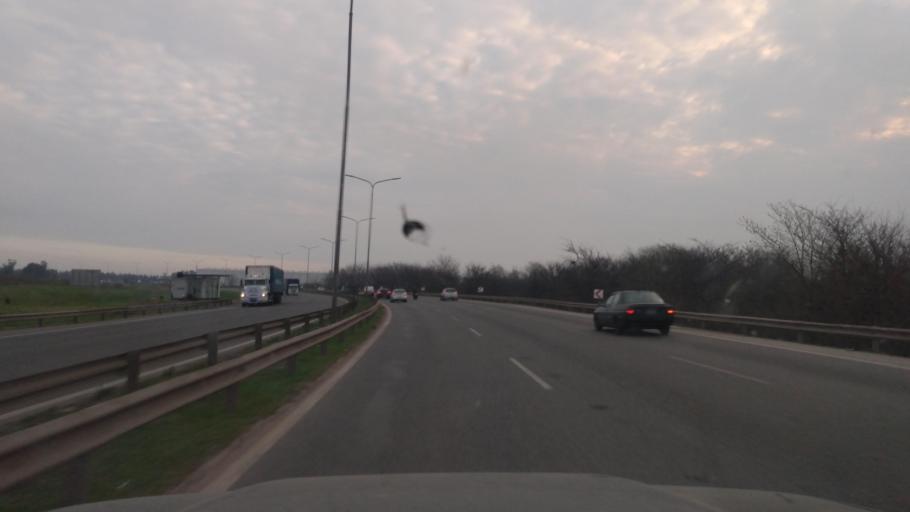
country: AR
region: Buenos Aires
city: Hurlingham
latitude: -34.5524
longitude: -58.6246
